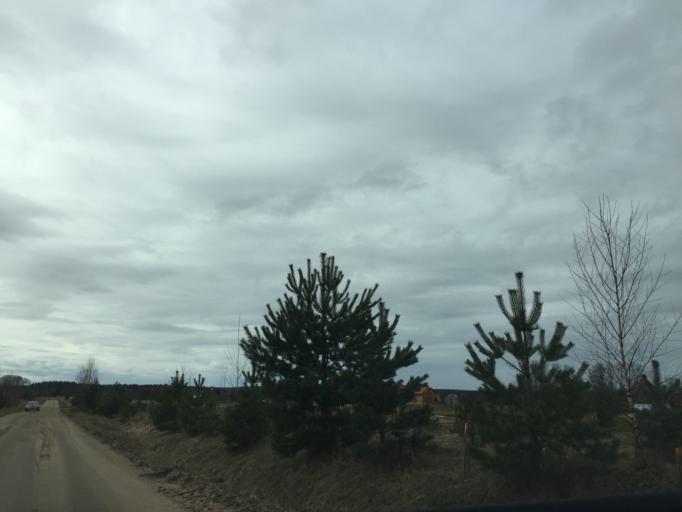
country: LV
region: Daugavpils
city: Daugavpils
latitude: 55.9174
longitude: 26.7394
